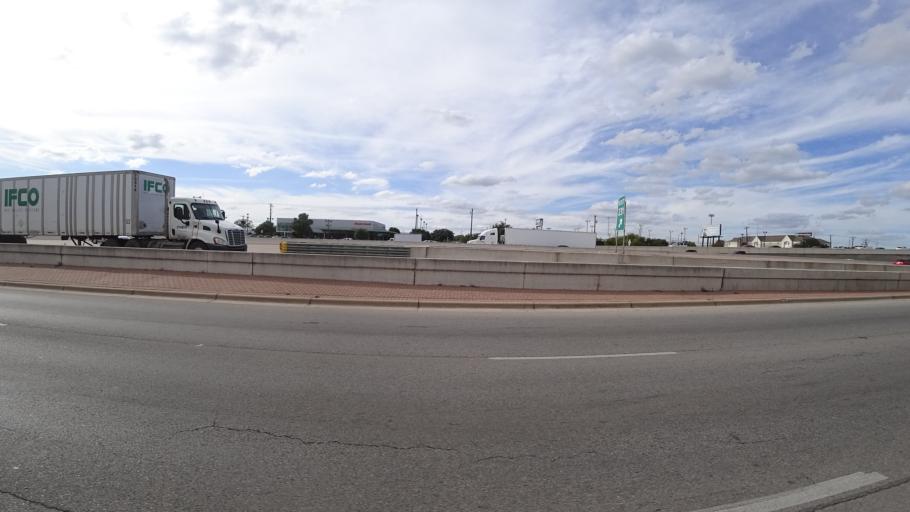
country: US
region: Texas
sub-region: Travis County
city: Austin
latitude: 30.2102
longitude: -97.7546
